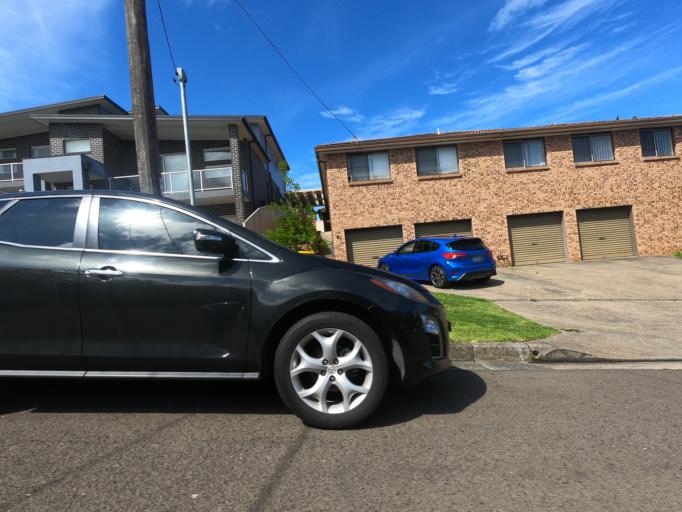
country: AU
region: New South Wales
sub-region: Wollongong
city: Lake Heights
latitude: -34.4805
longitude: 150.8710
